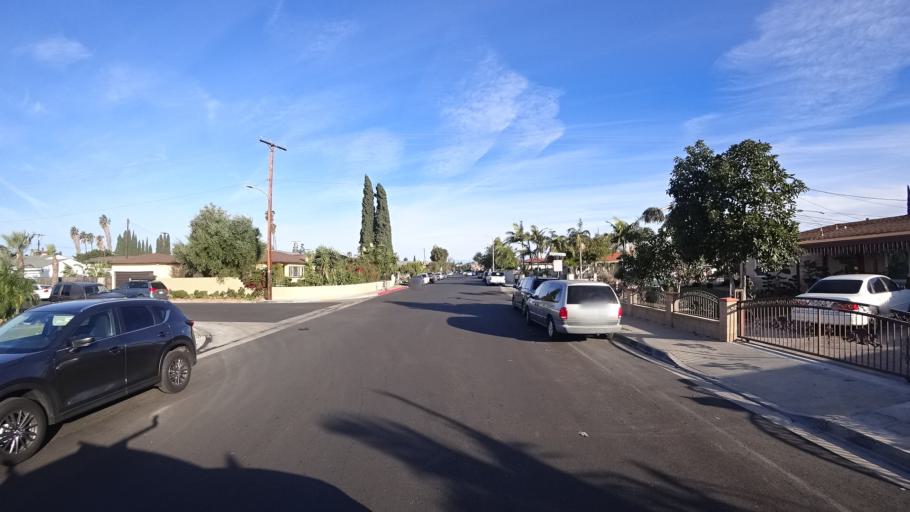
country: US
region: California
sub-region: Orange County
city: Garden Grove
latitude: 33.7696
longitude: -117.9446
